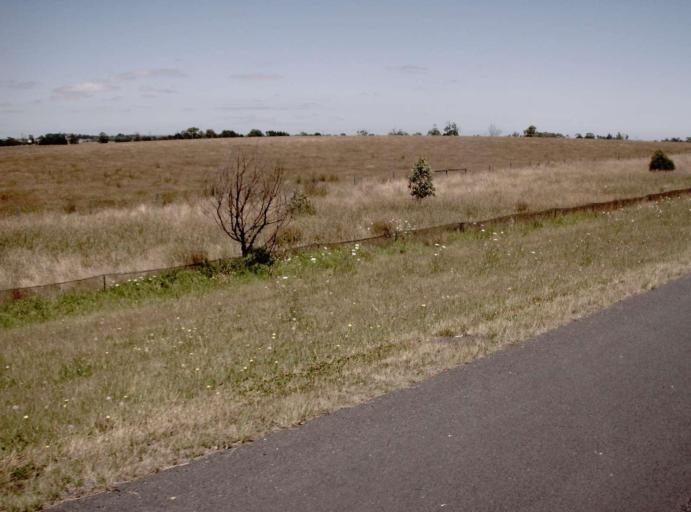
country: AU
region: Victoria
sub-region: Cardinia
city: Pakenham South
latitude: -38.0763
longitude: 145.5331
